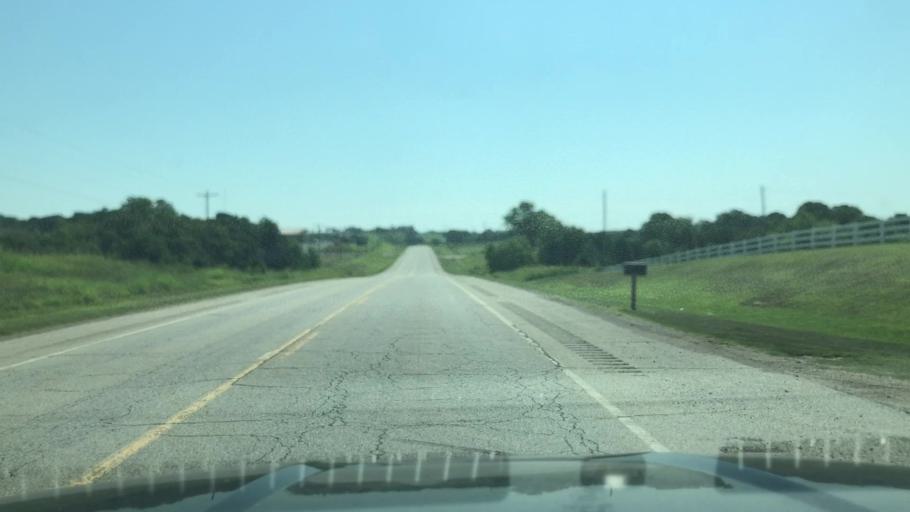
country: US
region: Oklahoma
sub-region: Creek County
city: Drumright
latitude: 35.9884
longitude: -96.5594
